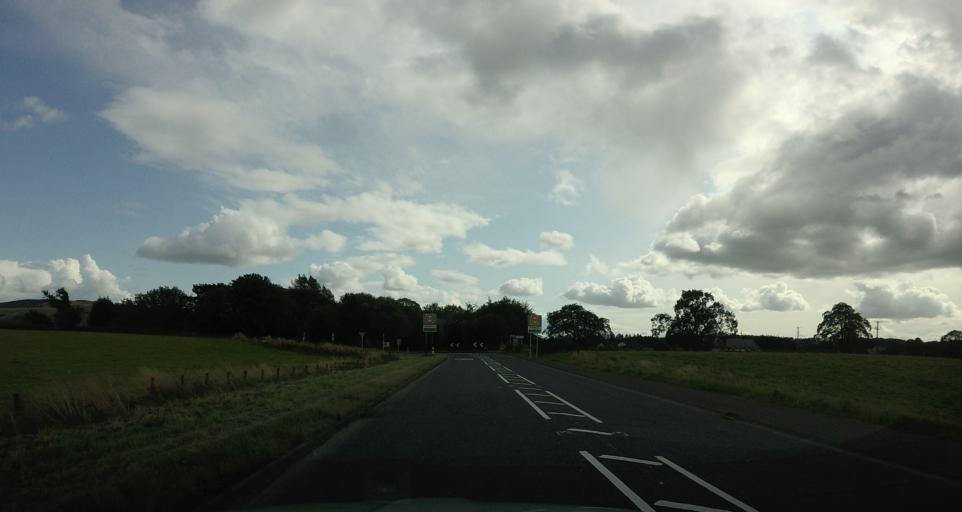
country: GB
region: Scotland
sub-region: Fife
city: Saline
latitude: 56.1696
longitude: -3.5814
